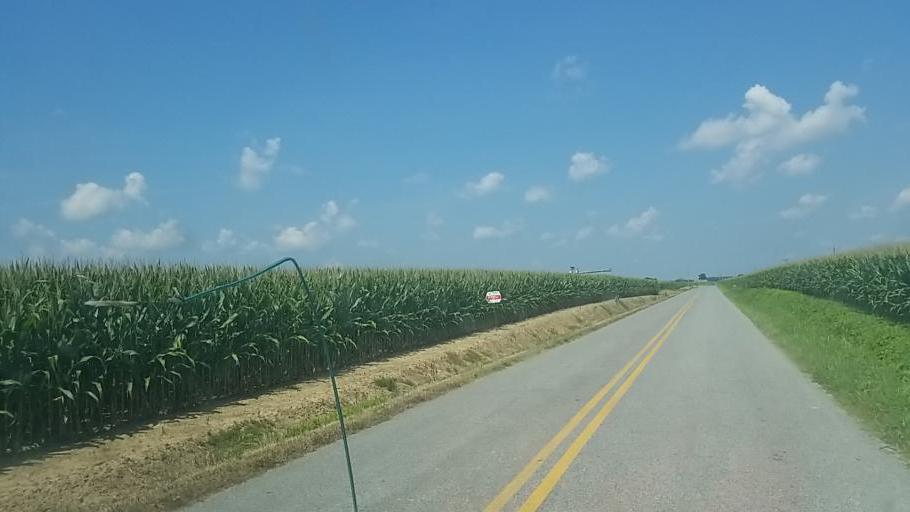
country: US
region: Maryland
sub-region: Worcester County
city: Berlin
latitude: 38.2853
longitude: -75.2345
